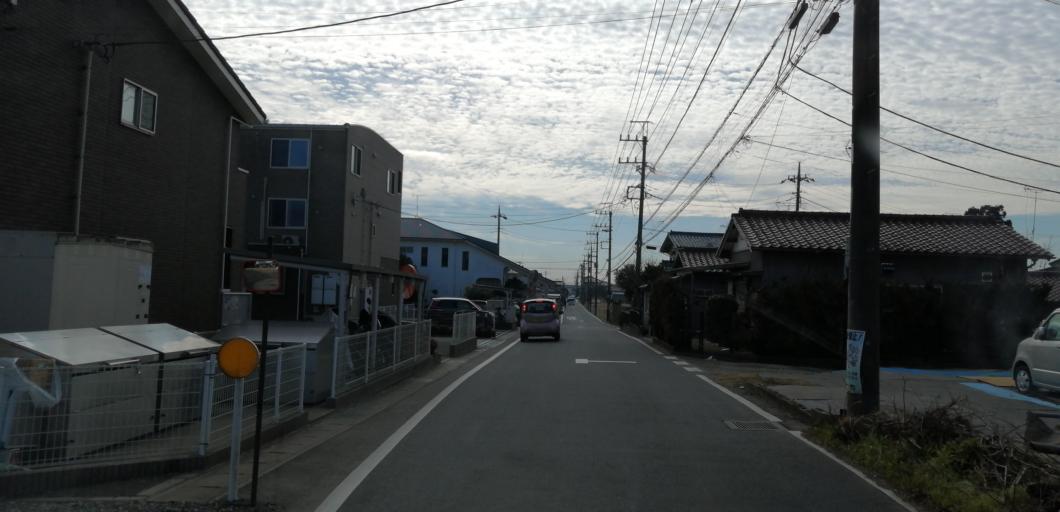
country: JP
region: Chiba
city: Narita
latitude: 35.7447
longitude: 140.3320
